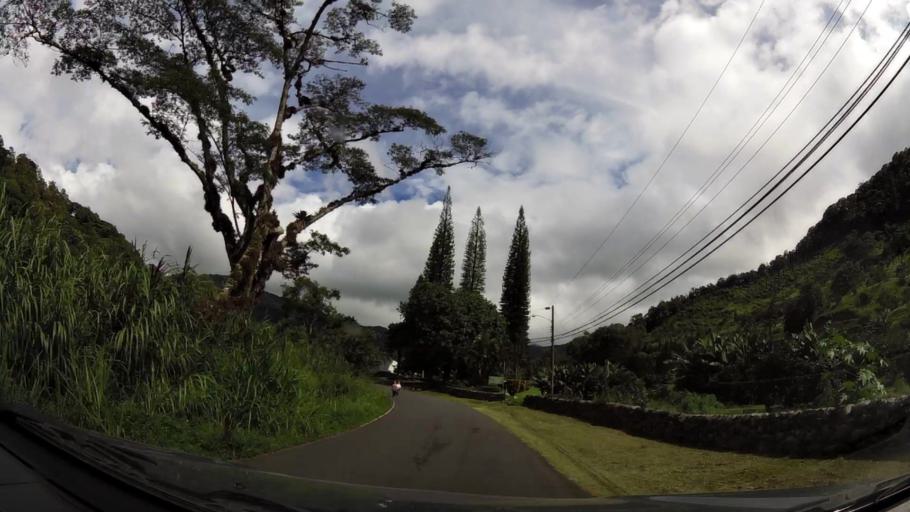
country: PA
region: Chiriqui
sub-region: Distrito Boquete
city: Boquete
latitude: 8.7936
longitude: -82.4284
